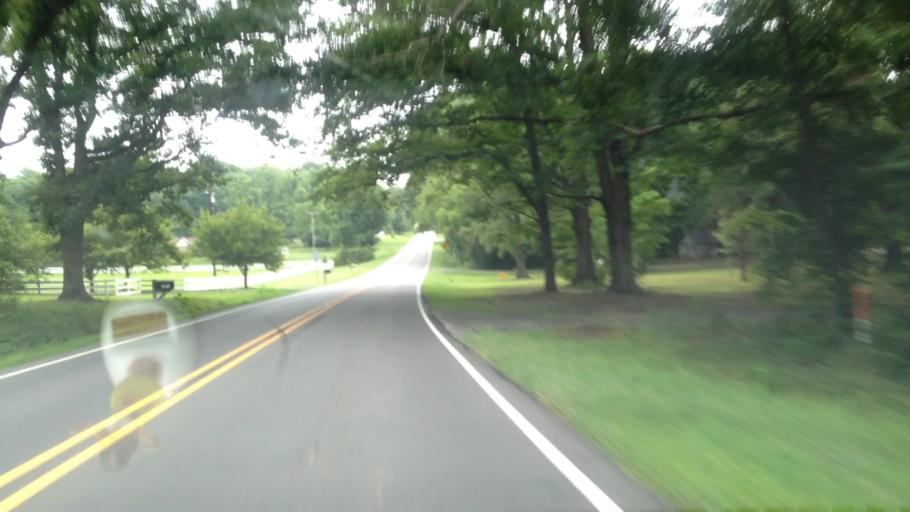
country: US
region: North Carolina
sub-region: Rockingham County
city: Mayodan
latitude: 36.4104
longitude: -80.0038
